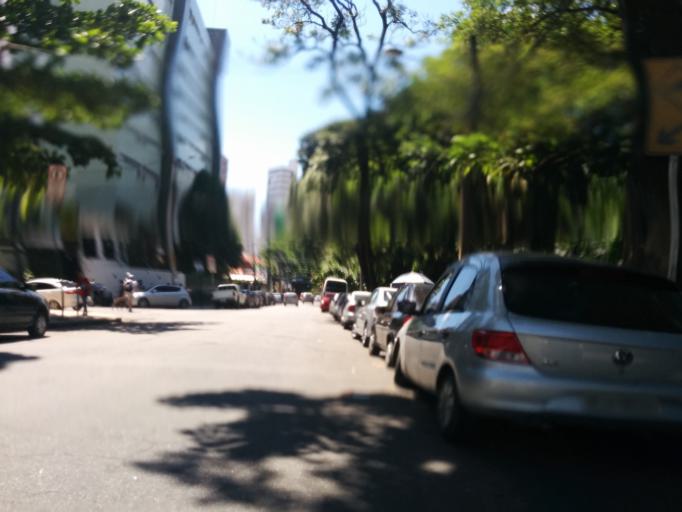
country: BR
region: Pernambuco
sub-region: Recife
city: Recife
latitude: -8.0363
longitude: -34.9038
